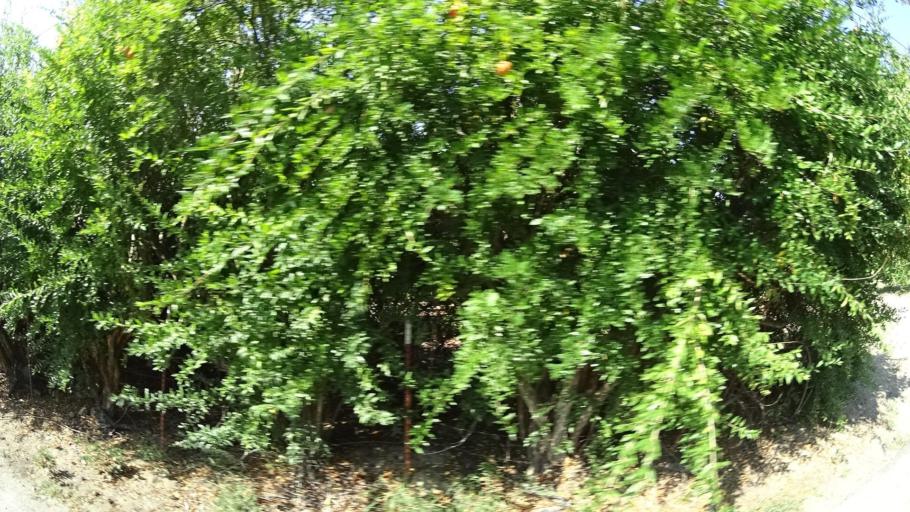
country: US
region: California
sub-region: San Diego County
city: Valley Center
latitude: 33.3392
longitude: -116.9925
